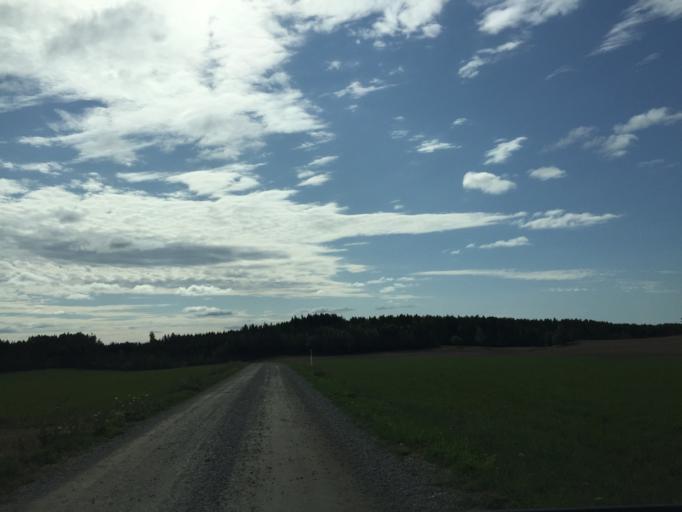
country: NO
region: Ostfold
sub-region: Hobol
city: Elvestad
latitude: 59.6333
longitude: 10.8886
